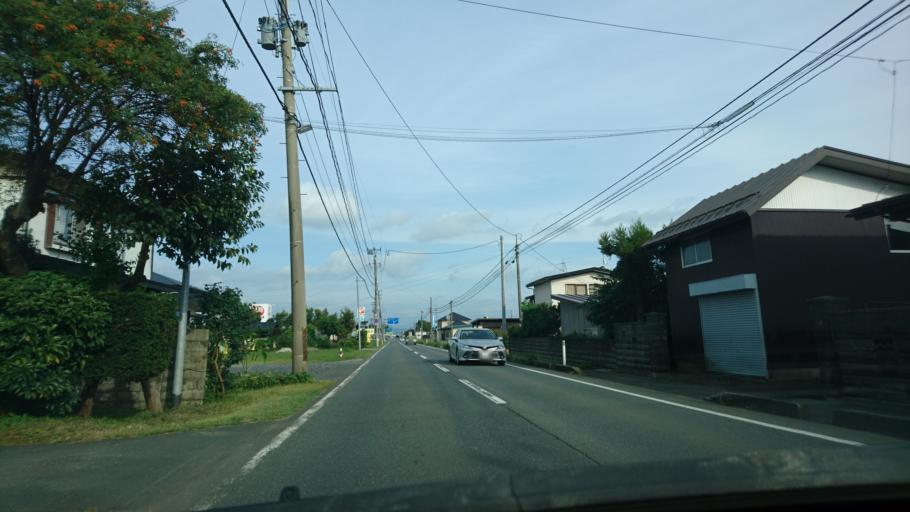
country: JP
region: Iwate
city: Kitakami
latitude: 39.3038
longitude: 141.0190
